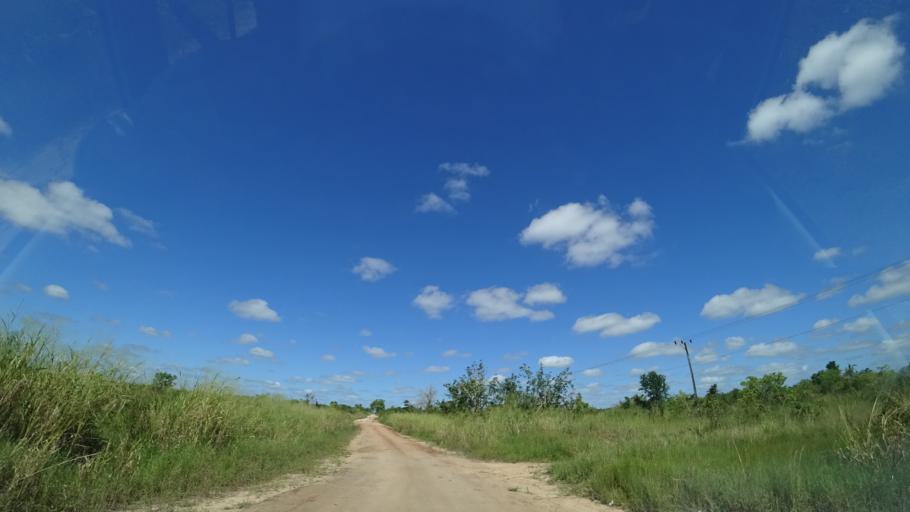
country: MZ
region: Sofala
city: Dondo
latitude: -19.3159
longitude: 34.6904
